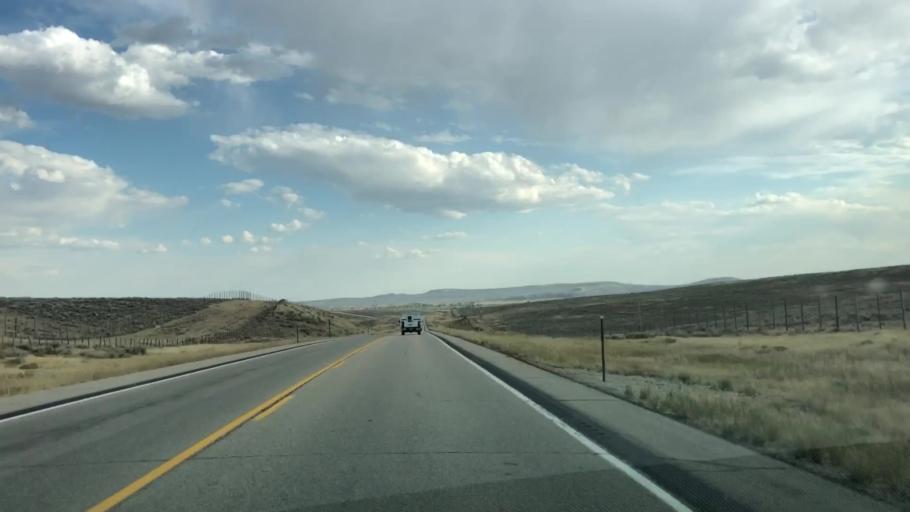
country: US
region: Wyoming
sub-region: Sublette County
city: Pinedale
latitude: 42.9120
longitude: -110.0782
